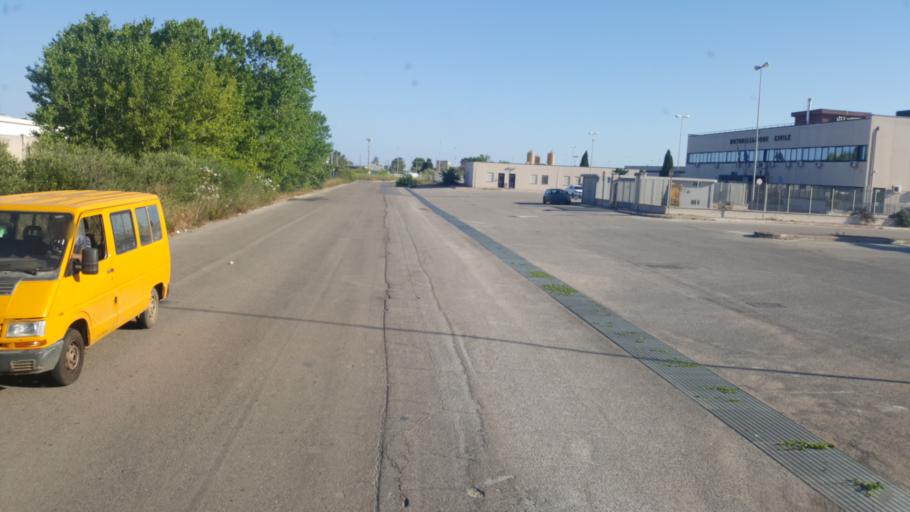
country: IT
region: Apulia
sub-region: Provincia di Brindisi
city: Materdomini
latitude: 40.6329
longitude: 17.9738
